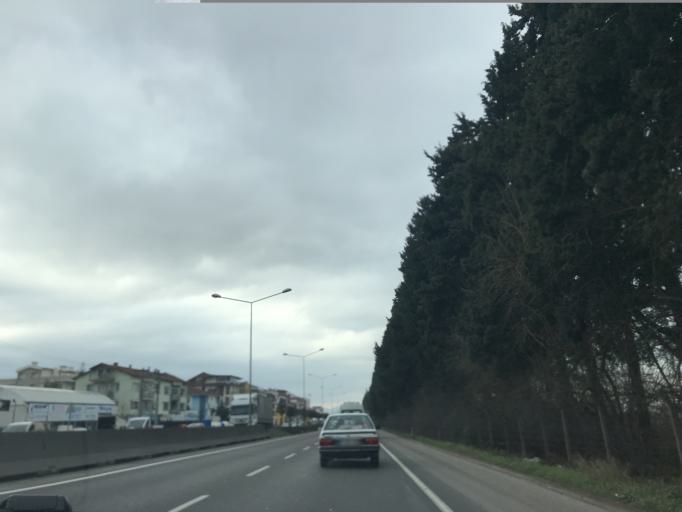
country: TR
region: Yalova
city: Yalova
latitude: 40.6593
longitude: 29.2985
